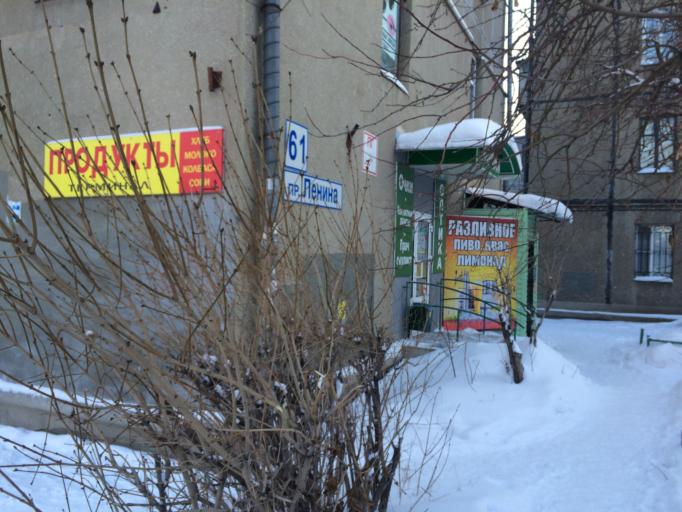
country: RU
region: Chelyabinsk
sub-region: Gorod Magnitogorsk
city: Magnitogorsk
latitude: 53.4151
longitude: 58.9850
